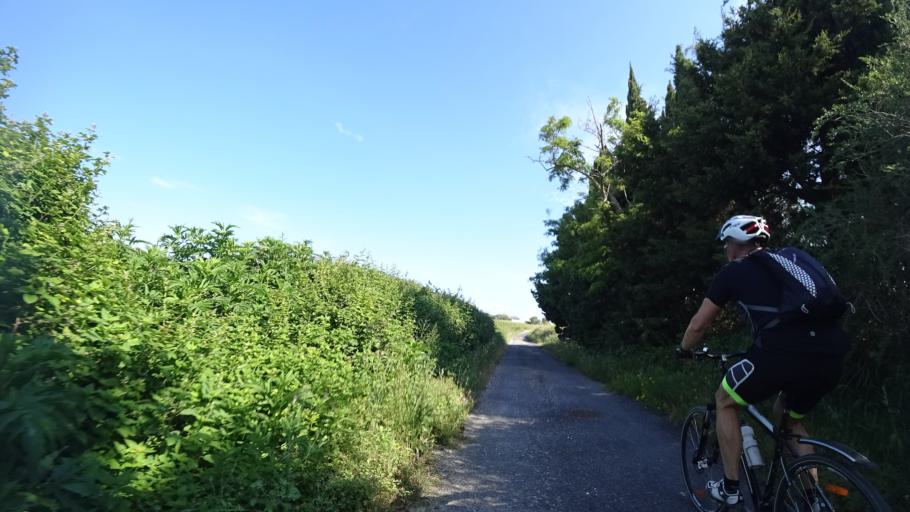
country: FR
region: Languedoc-Roussillon
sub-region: Departement de l'Herault
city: Olonzac
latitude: 43.2621
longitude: 2.7215
